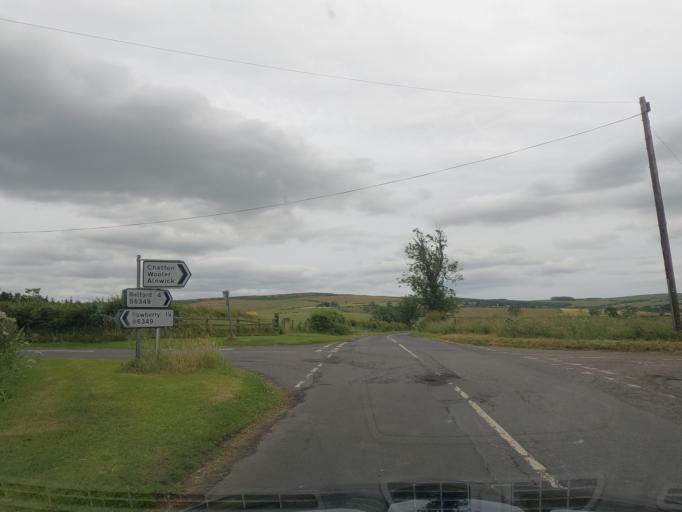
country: GB
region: England
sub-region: Northumberland
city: Belford
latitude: 55.5669
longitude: -1.9119
